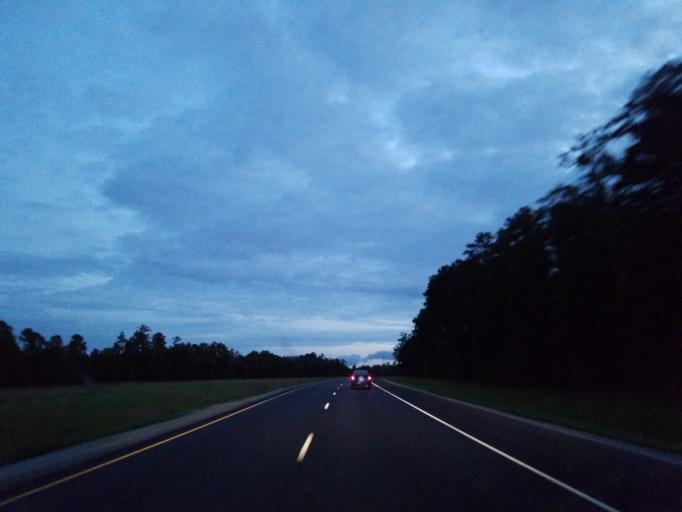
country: US
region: Mississippi
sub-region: Clarke County
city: Stonewall
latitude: 32.0217
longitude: -88.9236
